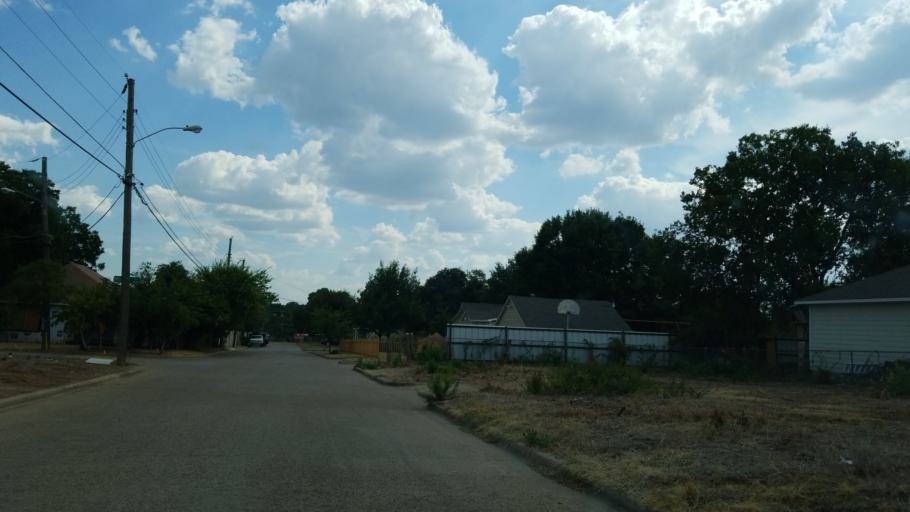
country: US
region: Texas
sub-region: Dallas County
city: Dallas
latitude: 32.7702
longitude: -96.8393
